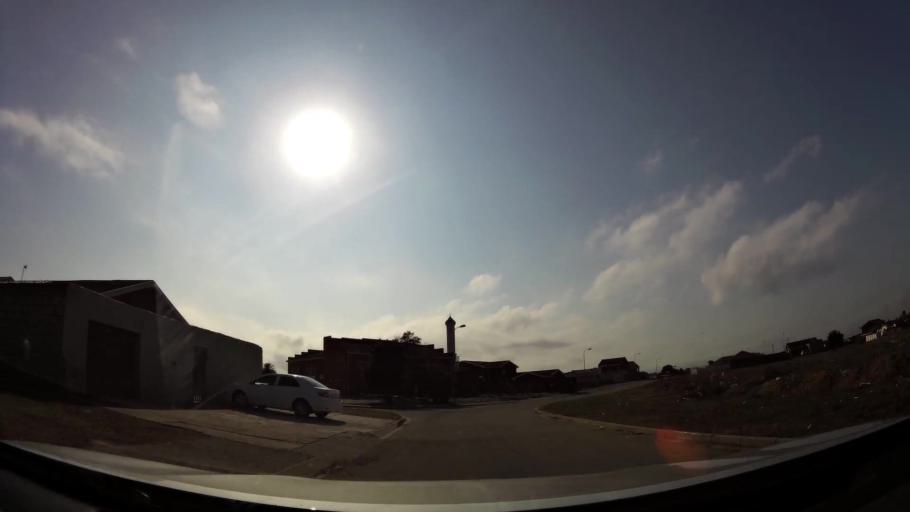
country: ZA
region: Eastern Cape
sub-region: Nelson Mandela Bay Metropolitan Municipality
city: Port Elizabeth
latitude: -33.9235
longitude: 25.5267
